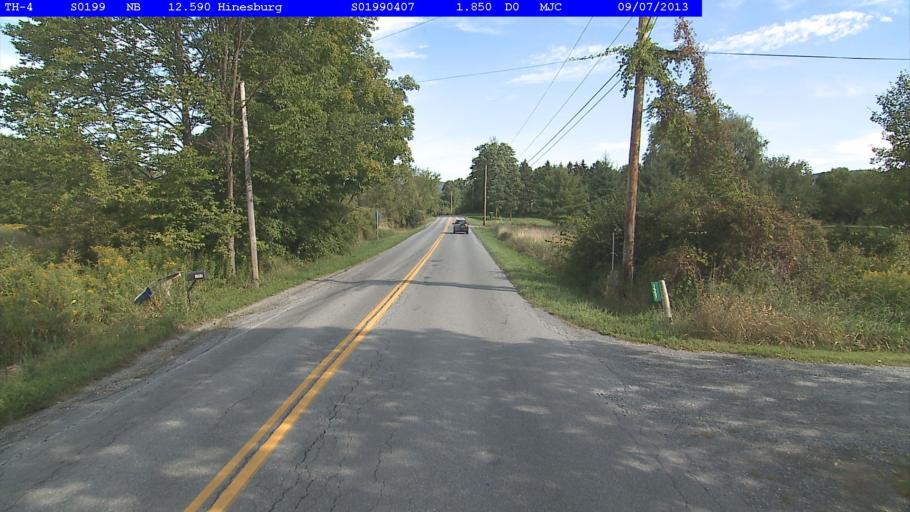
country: US
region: Vermont
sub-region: Chittenden County
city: Hinesburg
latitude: 44.3046
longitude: -73.1090
